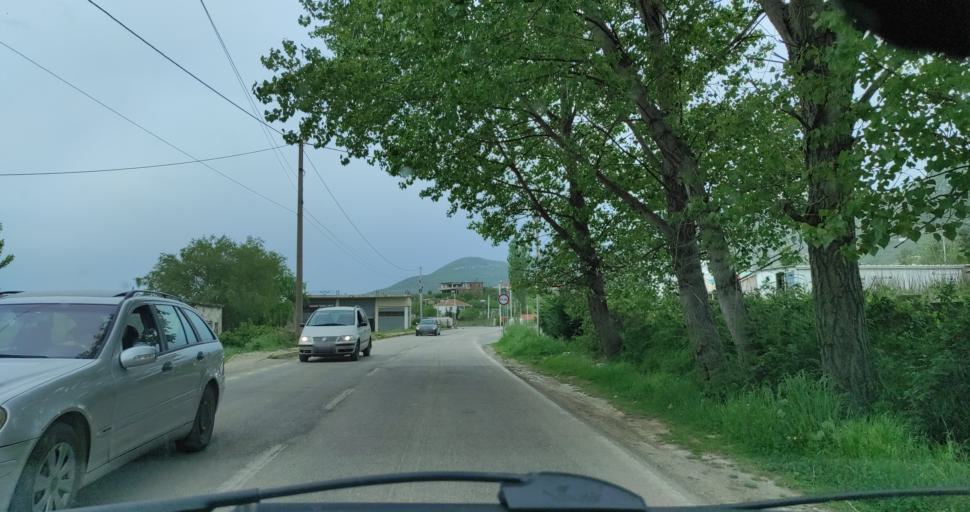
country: AL
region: Lezhe
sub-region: Rrethi i Kurbinit
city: Lac
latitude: 41.6148
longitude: 19.7116
